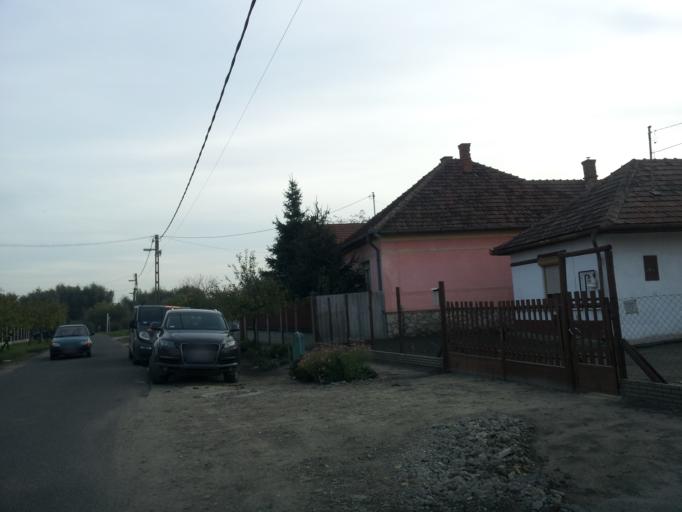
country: HU
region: Pest
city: Nagykata
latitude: 47.4113
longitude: 19.7496
